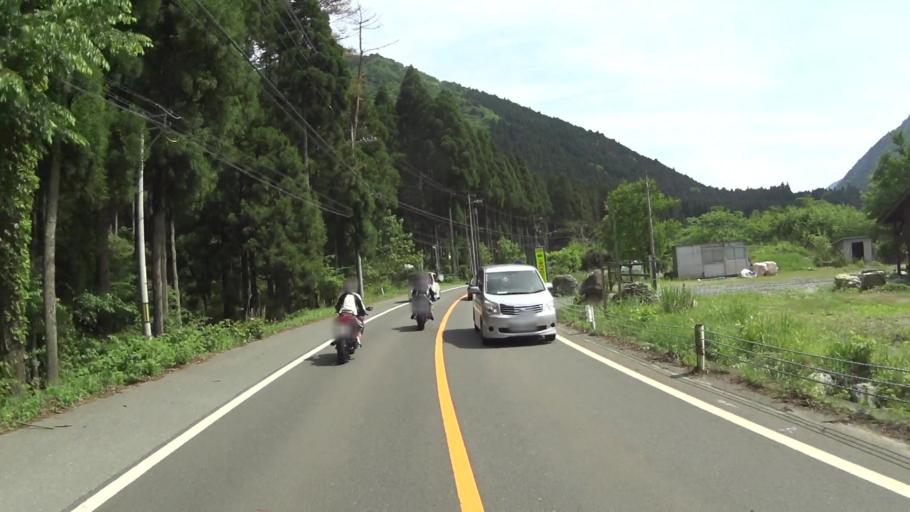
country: JP
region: Shiga Prefecture
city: Kitahama
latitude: 35.2882
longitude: 135.8850
